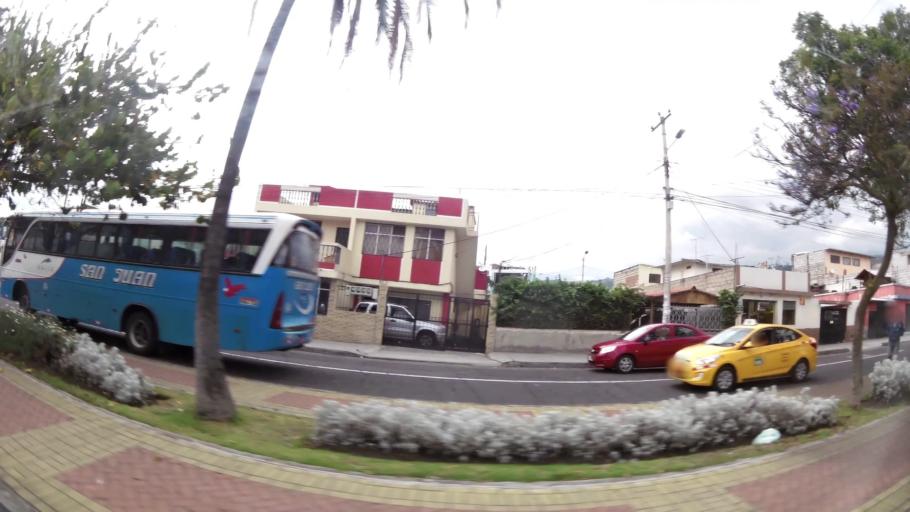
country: EC
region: Tungurahua
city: Ambato
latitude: -1.2338
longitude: -78.6175
